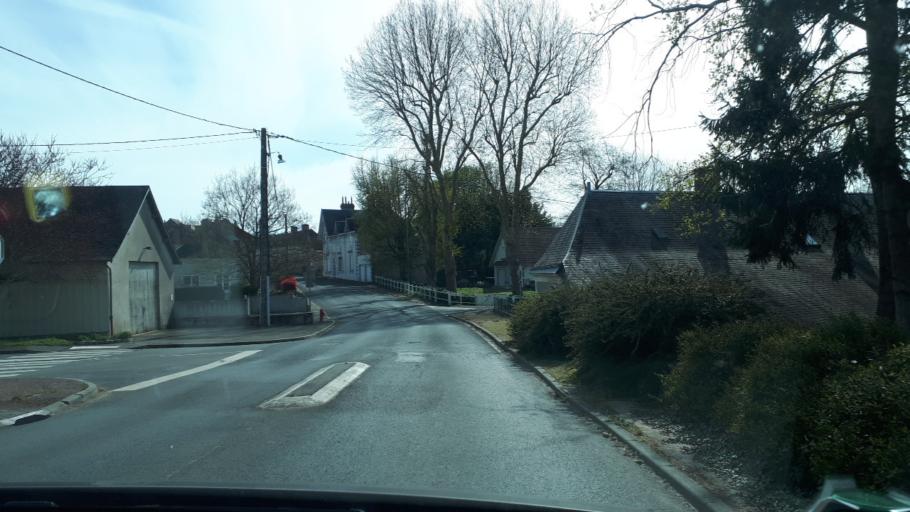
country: FR
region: Pays de la Loire
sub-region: Departement de la Sarthe
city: Yvre-le-Polin
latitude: 47.8182
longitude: 0.1503
